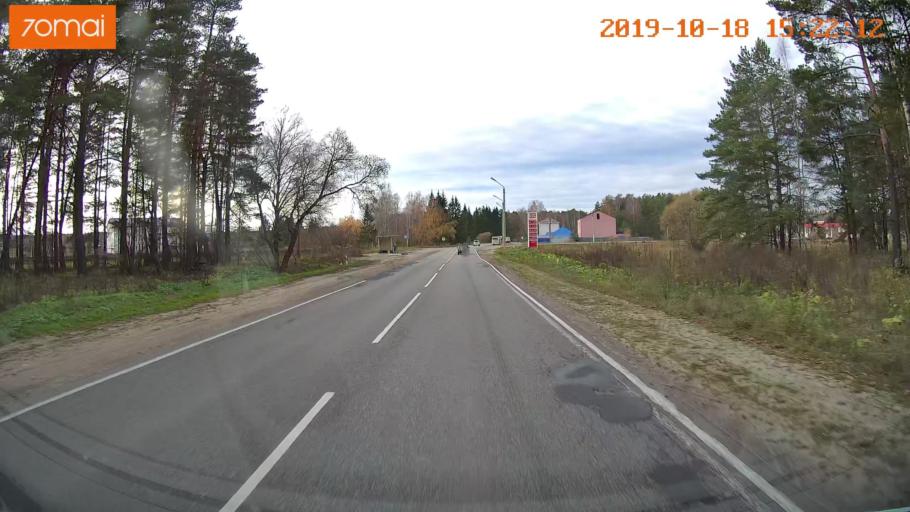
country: RU
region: Vladimir
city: Anopino
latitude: 55.7064
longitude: 40.7355
